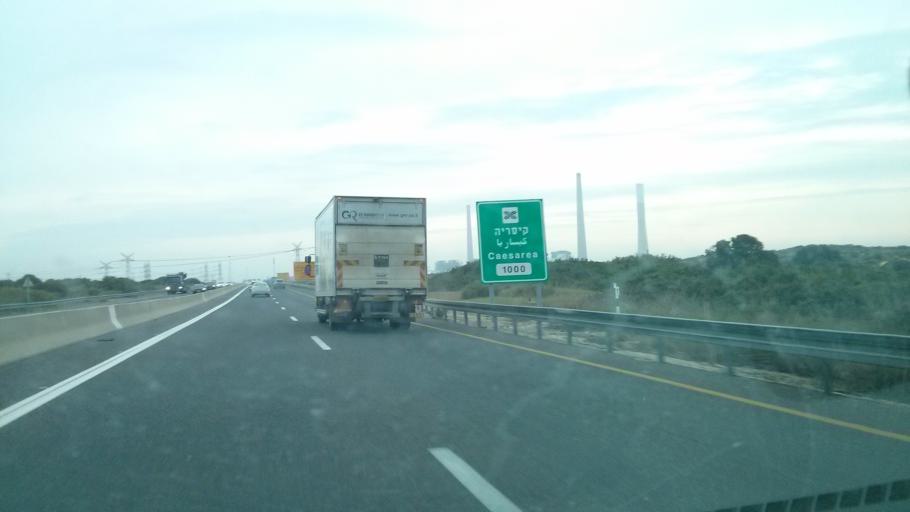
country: IL
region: Haifa
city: Qesarya
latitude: 32.4817
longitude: 34.9098
